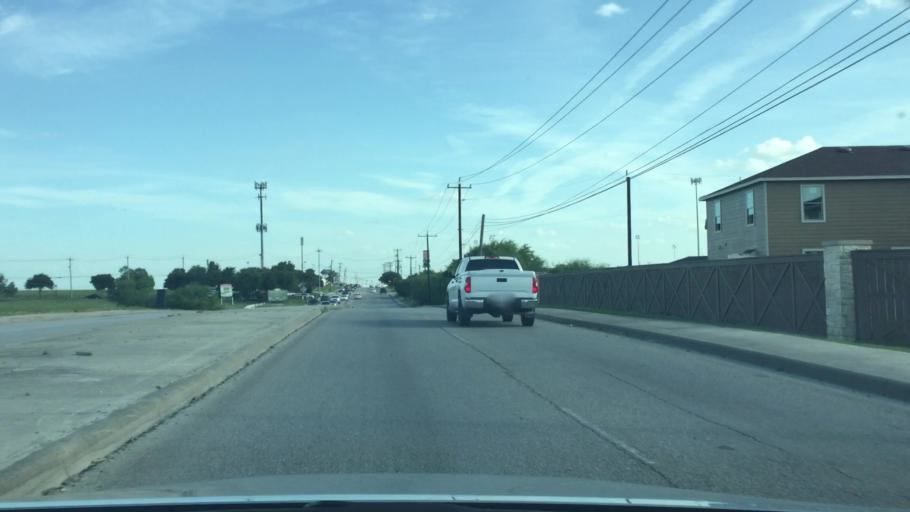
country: US
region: Texas
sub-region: Bexar County
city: Kirby
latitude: 29.4516
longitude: -98.3608
